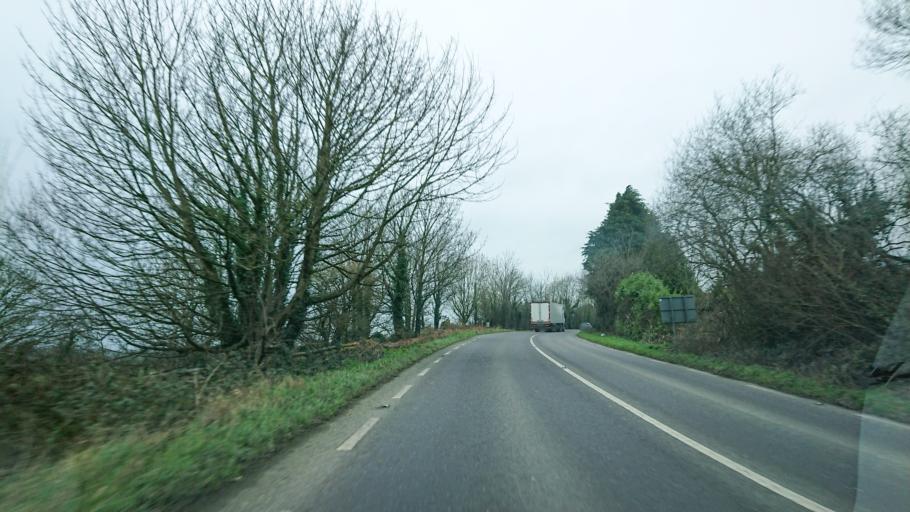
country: IE
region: Munster
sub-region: County Cork
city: Bandon
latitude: 51.7427
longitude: -8.8141
